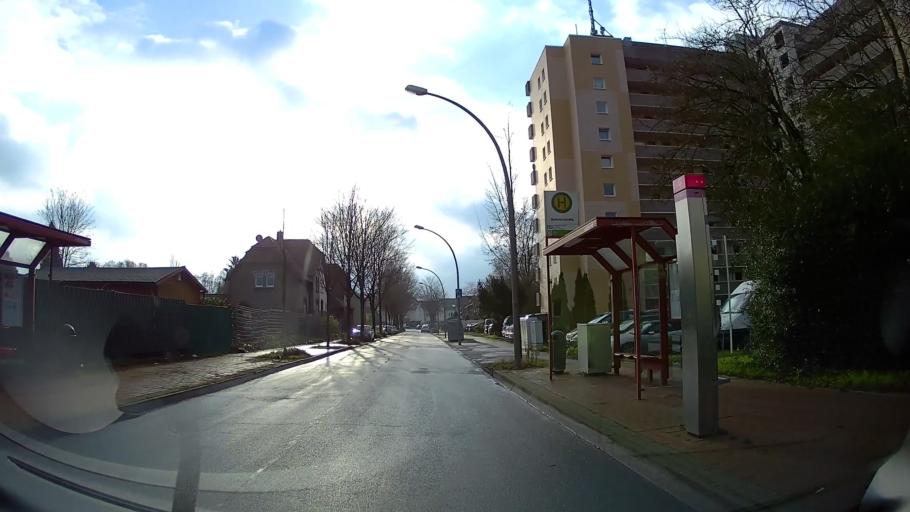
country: DE
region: North Rhine-Westphalia
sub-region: Regierungsbezirk Munster
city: Gladbeck
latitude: 51.5639
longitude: 6.9915
